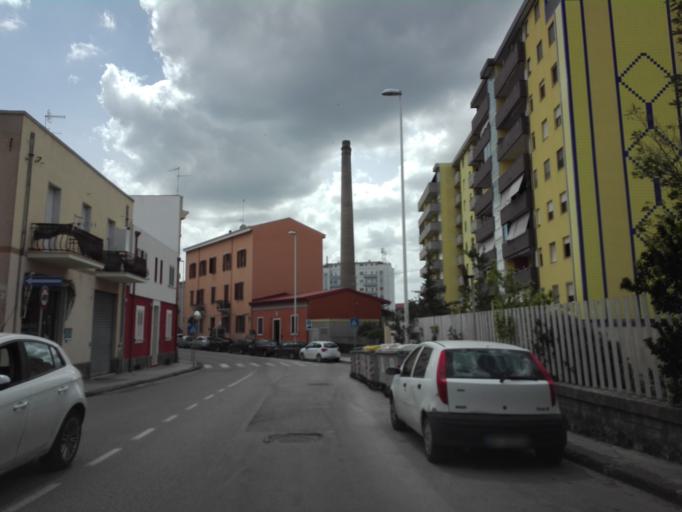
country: IT
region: Sardinia
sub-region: Provincia di Sassari
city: Sassari
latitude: 40.7337
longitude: 8.5566
